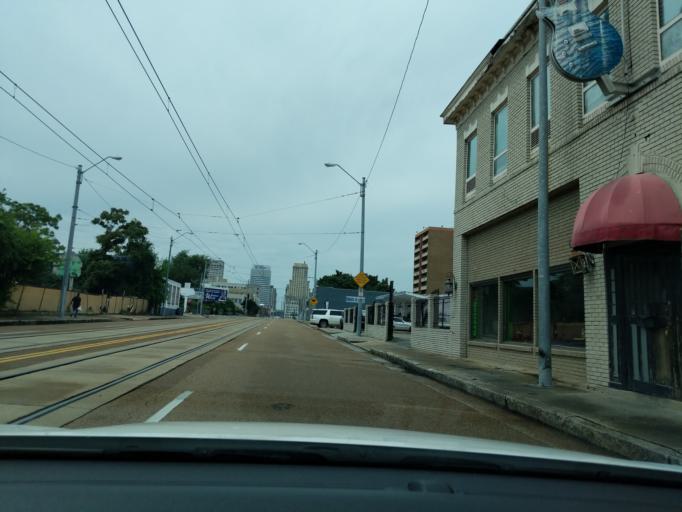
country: US
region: Tennessee
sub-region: Shelby County
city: Memphis
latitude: 35.1418
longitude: -90.0398
